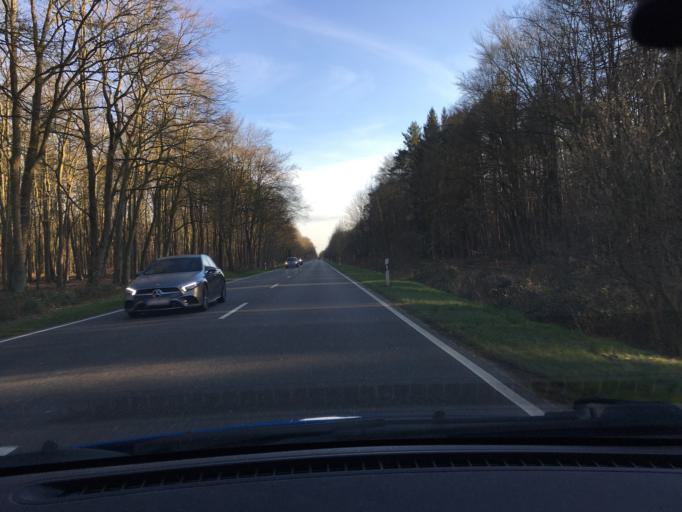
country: DE
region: Mecklenburg-Vorpommern
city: Feldstadt
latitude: 53.5704
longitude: 11.4370
